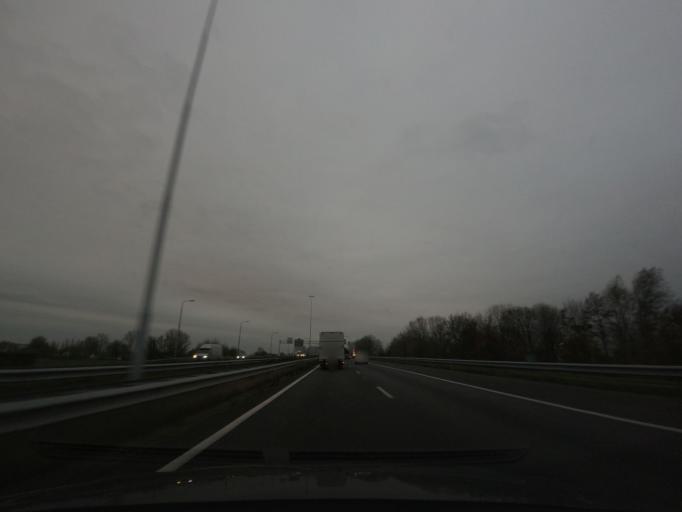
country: NL
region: North Brabant
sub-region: Gemeente Geertruidenberg
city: Geertruidenberg
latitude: 51.7240
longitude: 4.8925
